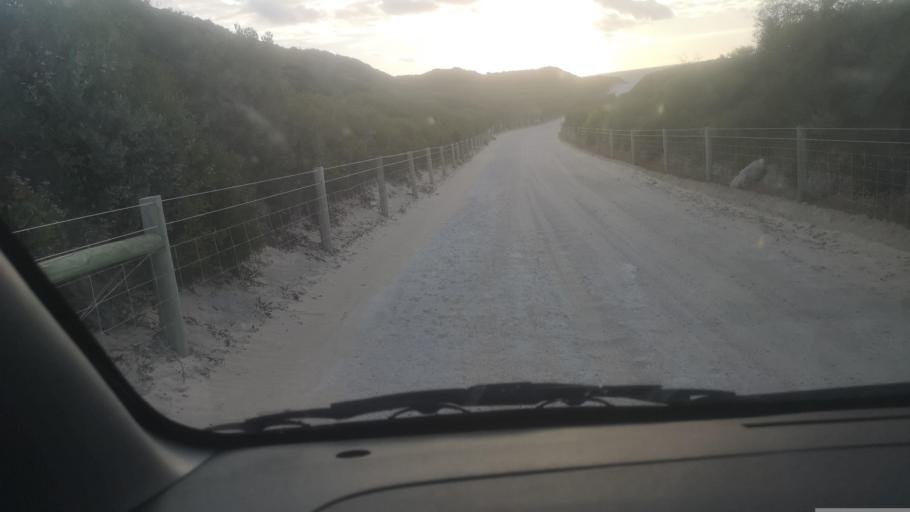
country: AU
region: Western Australia
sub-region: Wanneroo
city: Two Rocks
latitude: -31.5198
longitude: 115.6086
